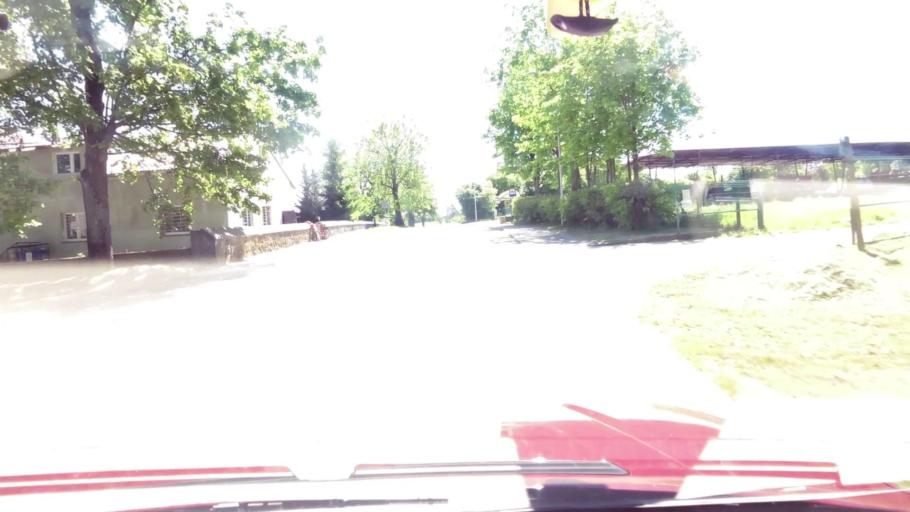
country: PL
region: West Pomeranian Voivodeship
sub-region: Powiat koszalinski
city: Bobolice
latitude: 54.0036
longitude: 16.6734
